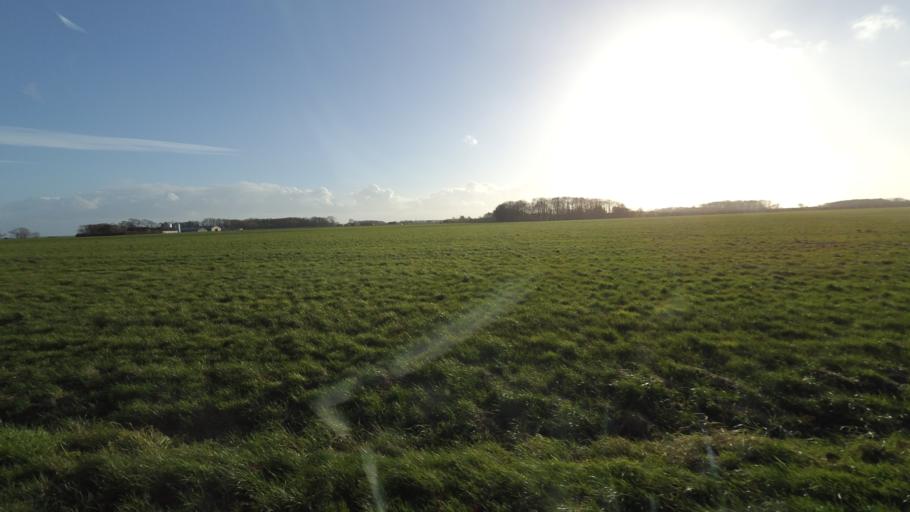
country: DK
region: Central Jutland
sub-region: Odder Kommune
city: Odder
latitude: 55.8788
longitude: 10.1815
